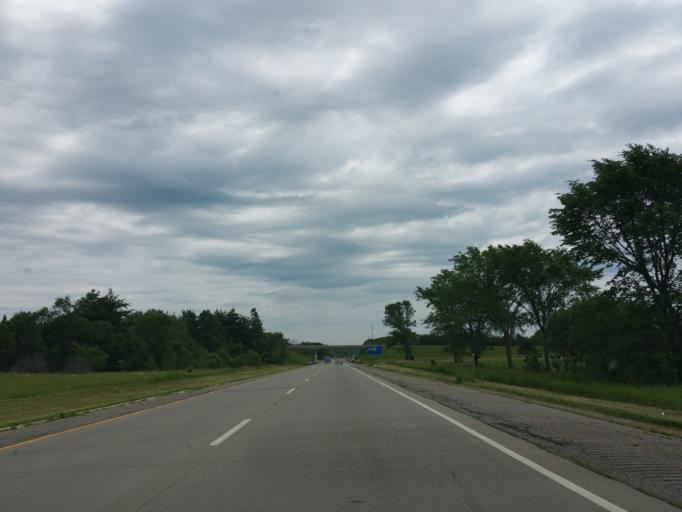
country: US
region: Wisconsin
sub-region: Juneau County
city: New Lisbon
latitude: 43.8952
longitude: -90.1758
